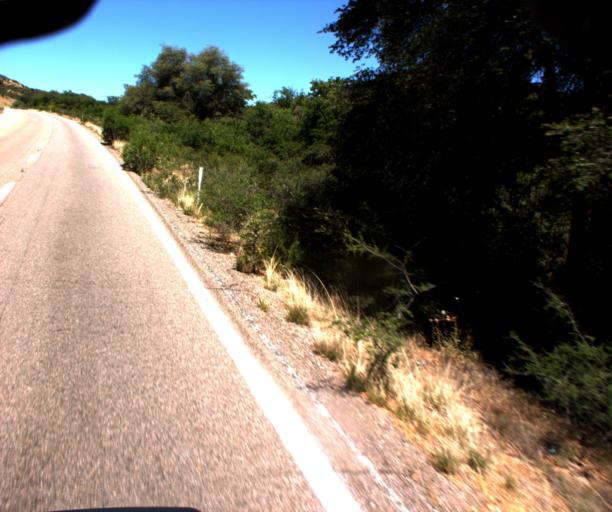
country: US
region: Arizona
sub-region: Gila County
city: Globe
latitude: 33.2260
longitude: -110.7891
